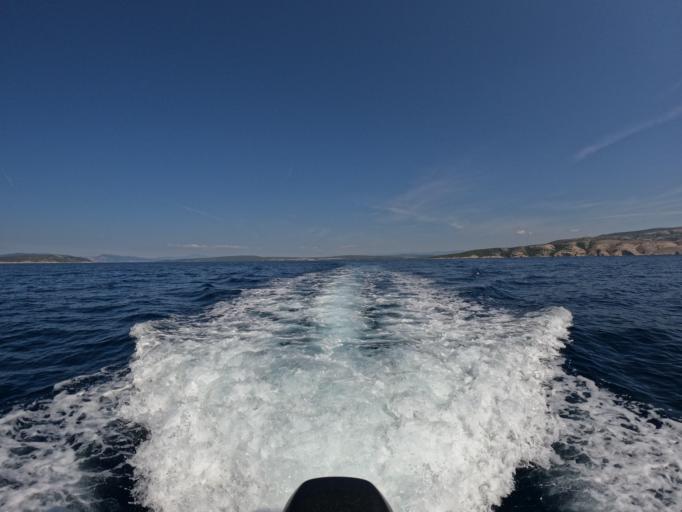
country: HR
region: Primorsko-Goranska
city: Punat
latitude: 44.9477
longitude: 14.6132
